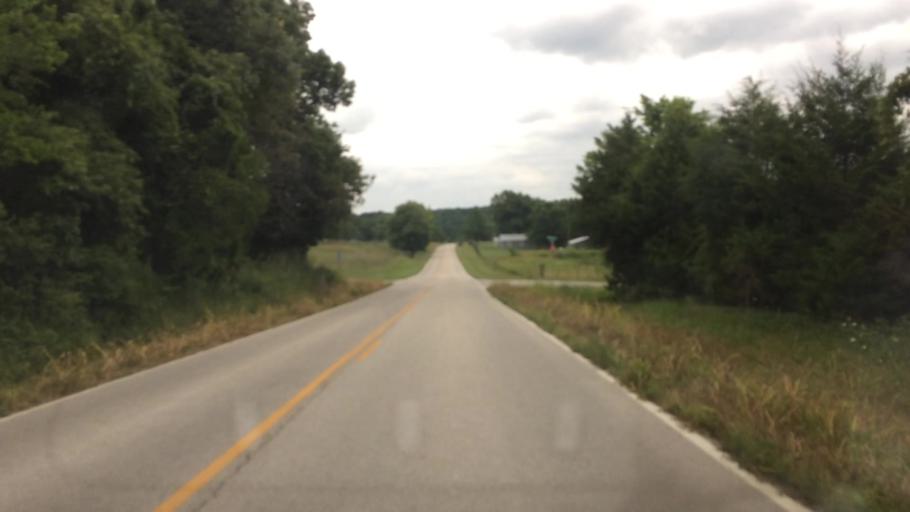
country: US
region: Missouri
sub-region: Greene County
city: Strafford
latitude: 37.2872
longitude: -93.0955
